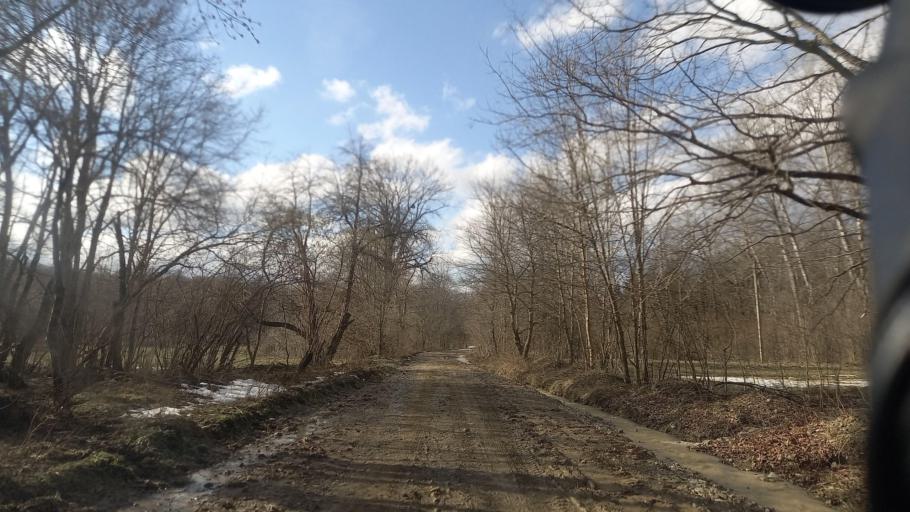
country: RU
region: Krasnodarskiy
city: Smolenskaya
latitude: 44.6001
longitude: 38.8777
